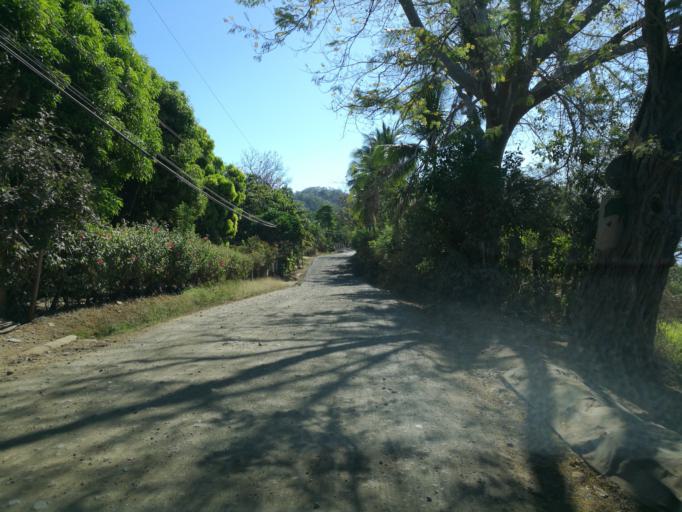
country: CR
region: Puntarenas
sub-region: Canton Central de Puntarenas
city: Puntarenas
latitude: 10.0953
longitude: -84.9807
